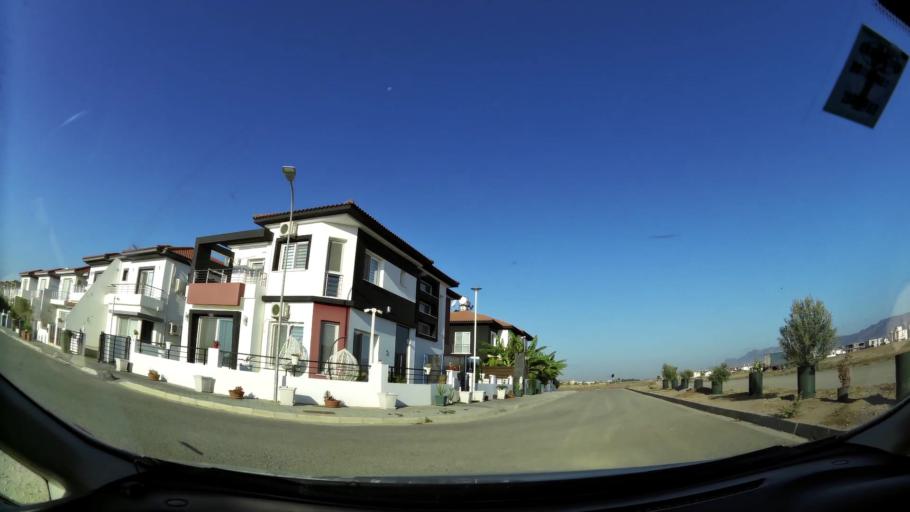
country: CY
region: Lefkosia
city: Nicosia
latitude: 35.2042
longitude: 33.2951
